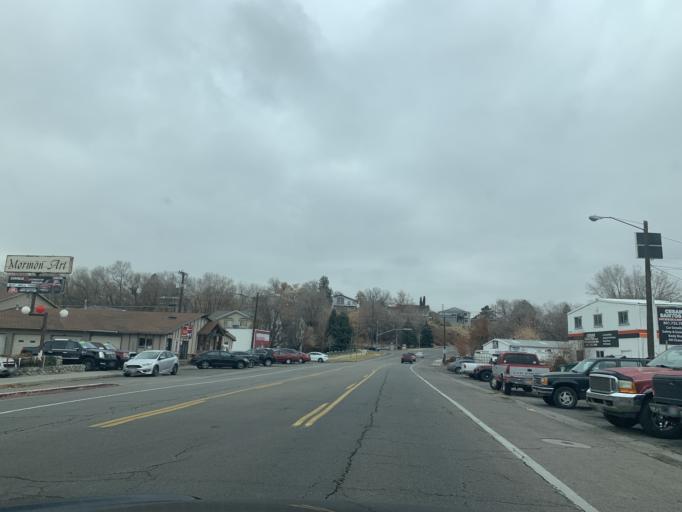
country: US
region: Utah
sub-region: Utah County
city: Provo
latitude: 40.2534
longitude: -111.6726
